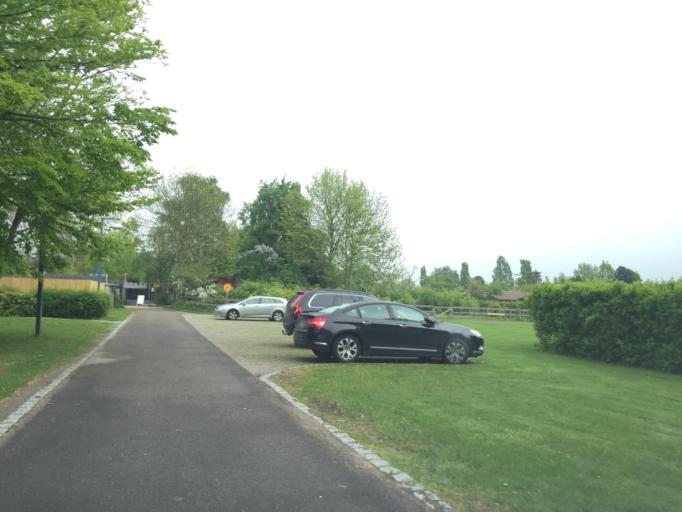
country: DK
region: Capital Region
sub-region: Rodovre Kommune
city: Rodovre
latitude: 55.6774
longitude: 12.4426
